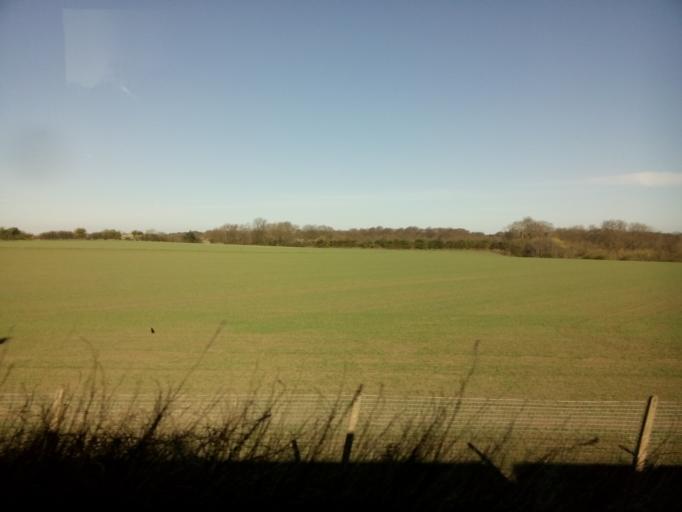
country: GB
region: England
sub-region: Northumberland
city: Hebron
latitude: 55.1699
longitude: -1.6668
